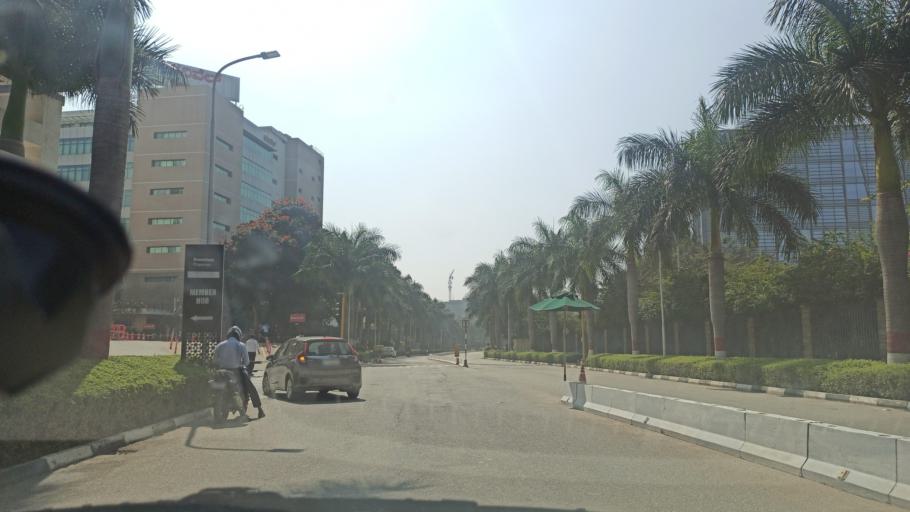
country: IN
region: Karnataka
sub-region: Bangalore Urban
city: Bangalore
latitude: 12.9260
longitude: 77.6858
